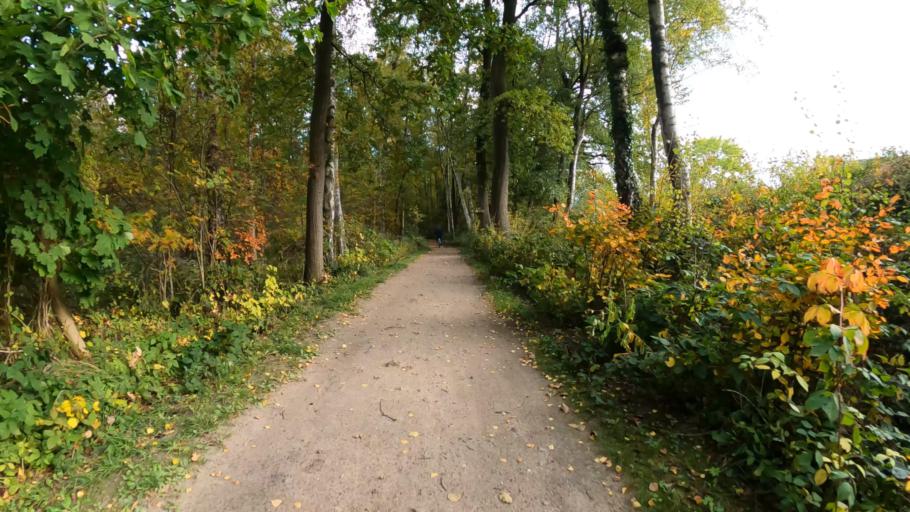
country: DE
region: Schleswig-Holstein
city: Ahrensburg
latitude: 53.6672
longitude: 10.2059
